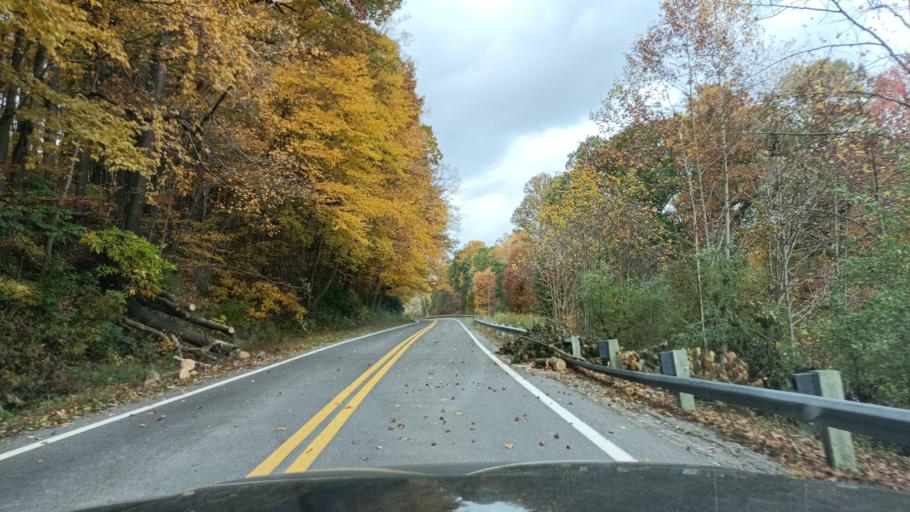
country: US
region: West Virginia
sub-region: Monongalia County
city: Cheat Lake
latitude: 39.6552
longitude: -79.7466
